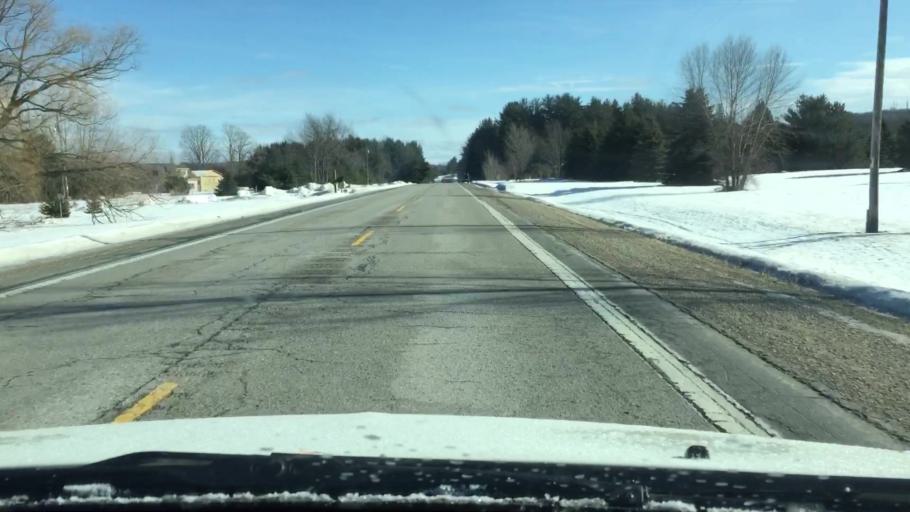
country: US
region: Michigan
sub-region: Charlevoix County
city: East Jordan
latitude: 45.0991
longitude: -85.1106
